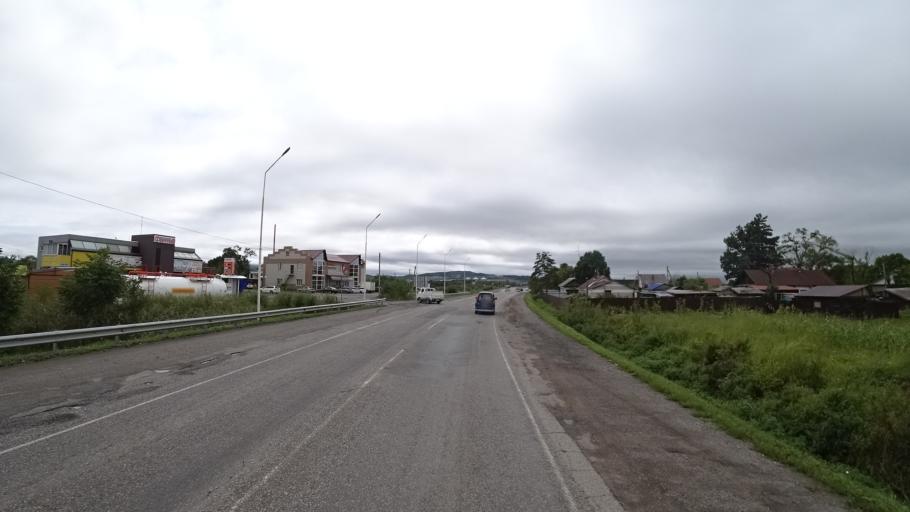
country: RU
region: Primorskiy
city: Monastyrishche
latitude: 44.2020
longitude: 132.4501
